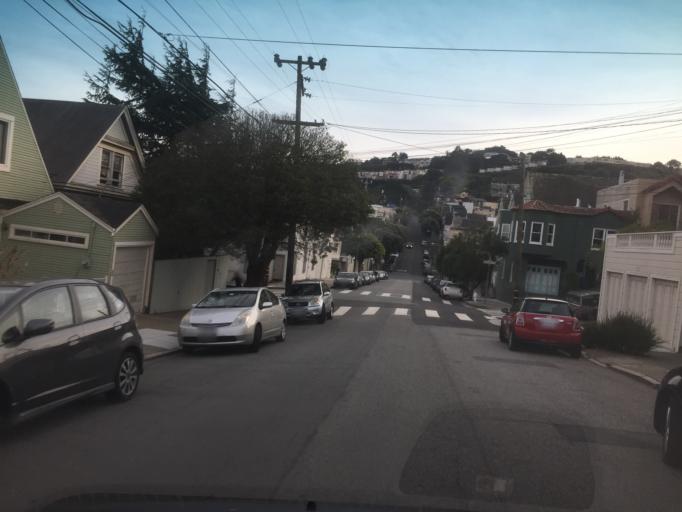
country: US
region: California
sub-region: San Francisco County
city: San Francisco
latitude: 37.7520
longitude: -122.4407
